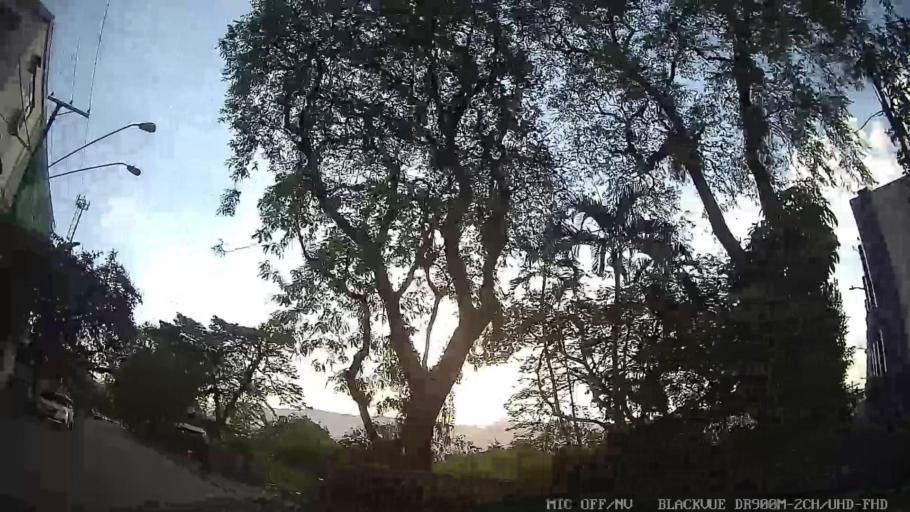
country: BR
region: Sao Paulo
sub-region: Cubatao
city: Cubatao
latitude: -23.8913
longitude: -46.4216
